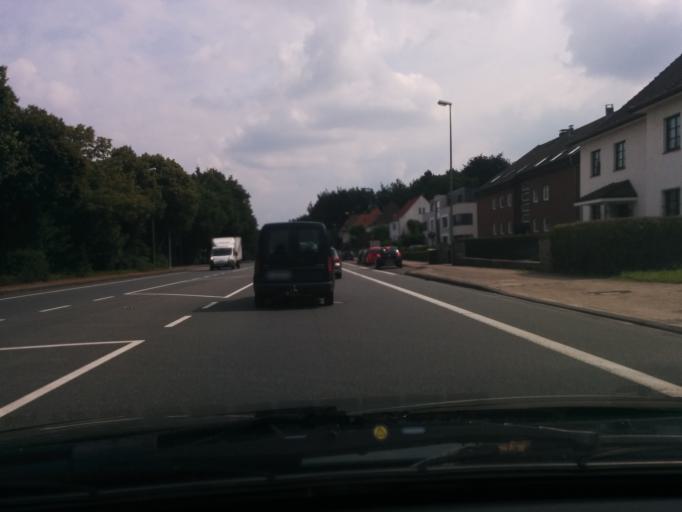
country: DE
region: North Rhine-Westphalia
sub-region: Regierungsbezirk Detmold
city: Bielefeld
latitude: 52.0318
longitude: 8.5009
